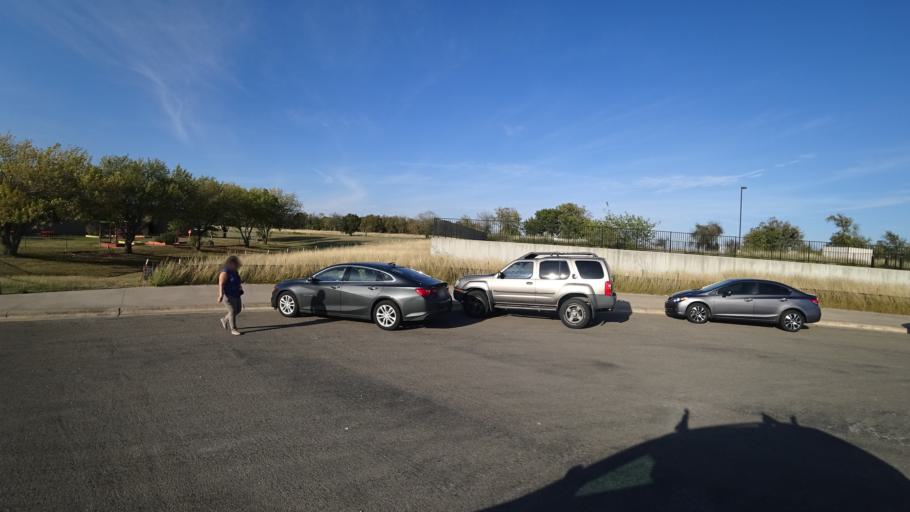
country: US
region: Texas
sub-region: Travis County
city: Pflugerville
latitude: 30.4011
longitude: -97.6428
